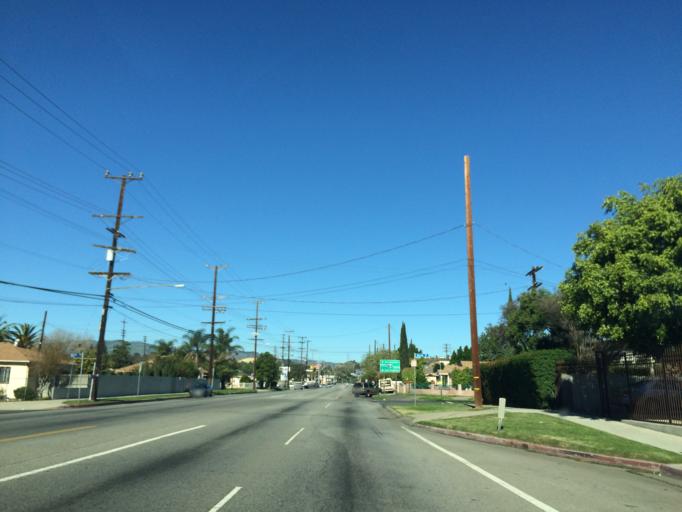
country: US
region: California
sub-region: Los Angeles County
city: San Fernando
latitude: 34.2759
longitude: -118.4502
